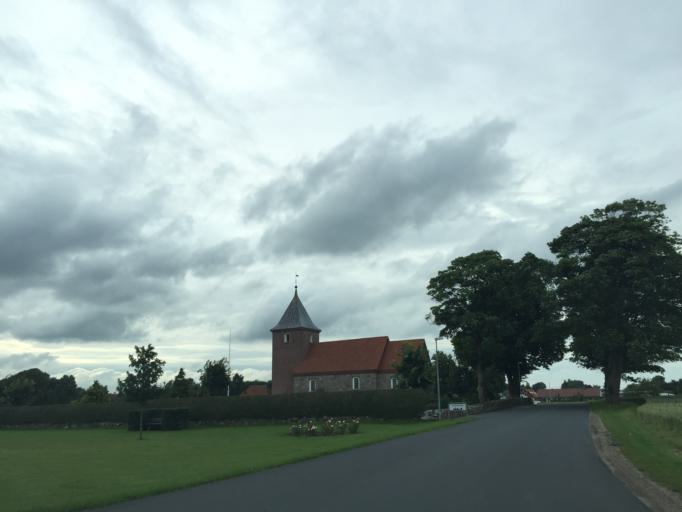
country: DK
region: Central Jutland
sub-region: Silkeborg Kommune
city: Silkeborg
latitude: 56.2354
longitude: 9.5469
